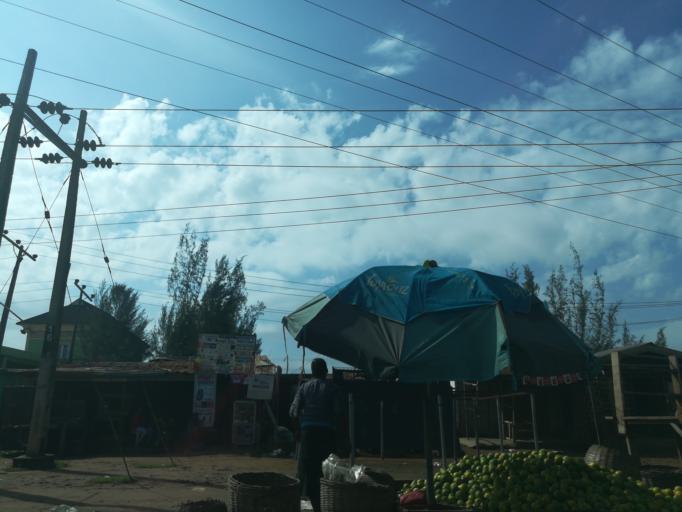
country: NG
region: Lagos
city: Ikorodu
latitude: 6.6280
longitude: 3.5092
